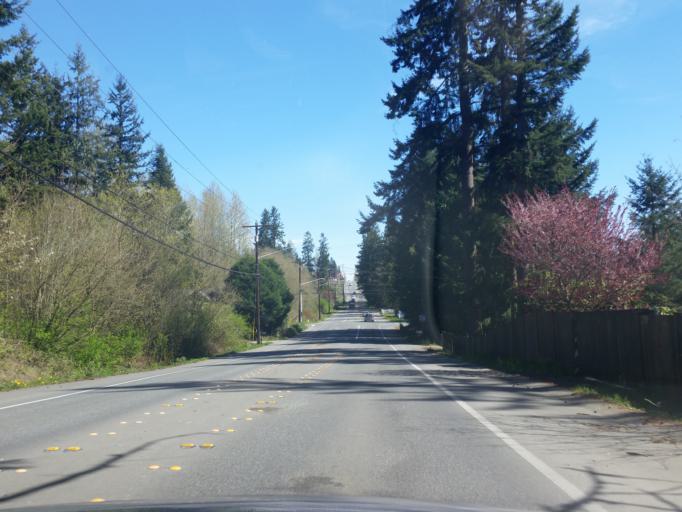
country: US
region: Washington
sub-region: Snohomish County
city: Clearview
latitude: 47.8339
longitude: -122.1356
